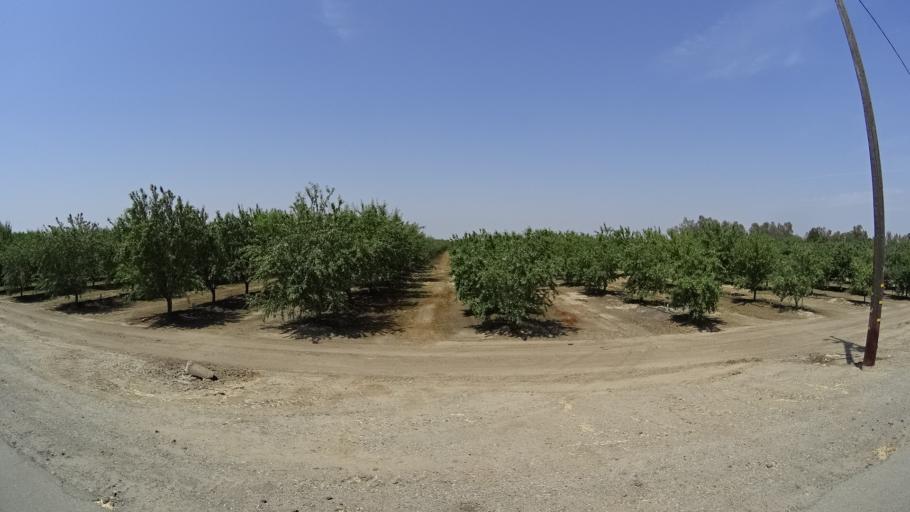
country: US
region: California
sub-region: Kings County
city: Lemoore
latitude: 36.3374
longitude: -119.7808
